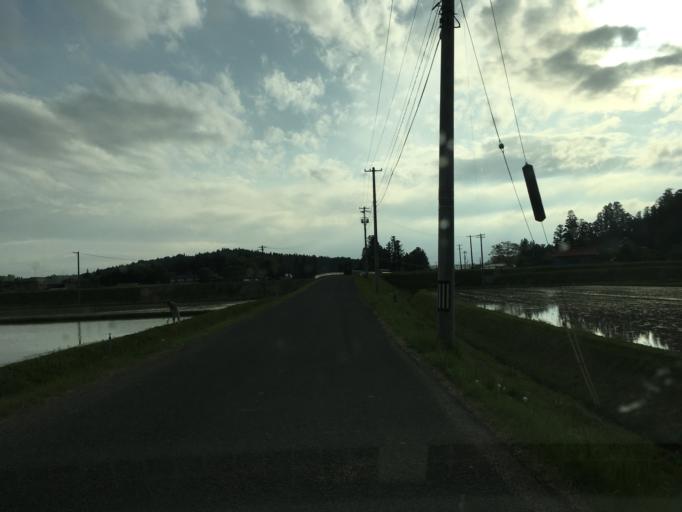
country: JP
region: Iwate
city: Ichinoseki
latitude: 38.8110
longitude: 141.1846
